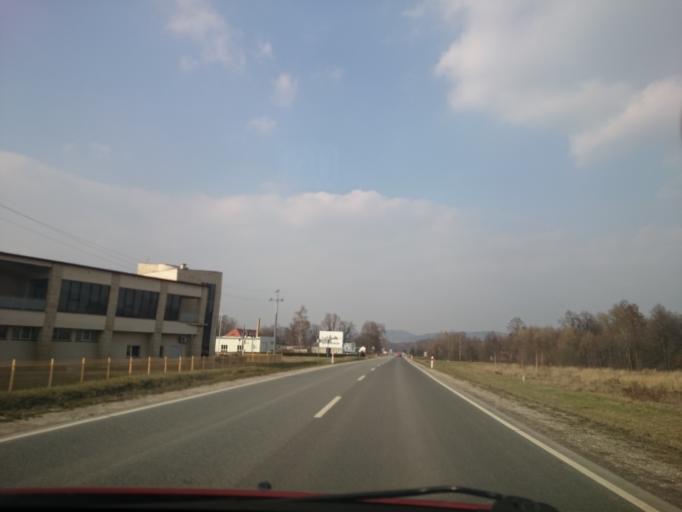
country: PL
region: Lower Silesian Voivodeship
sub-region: Powiat klodzki
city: Bystrzyca Klodzka
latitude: 50.3072
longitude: 16.6601
